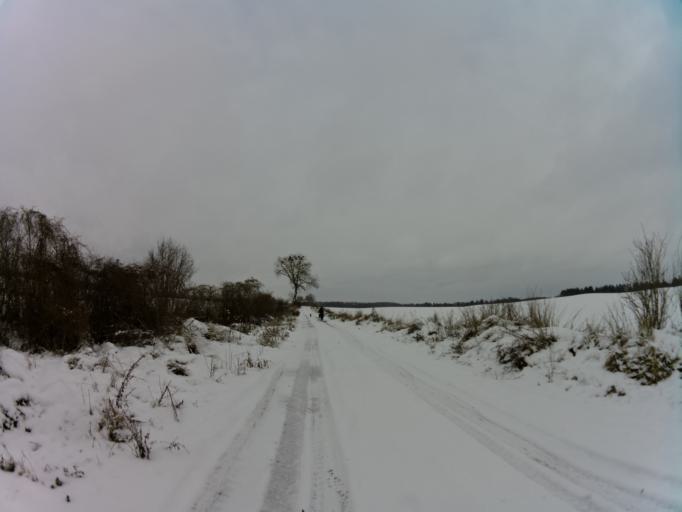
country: PL
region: West Pomeranian Voivodeship
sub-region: Powiat choszczenski
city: Recz
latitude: 53.2753
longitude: 15.5339
